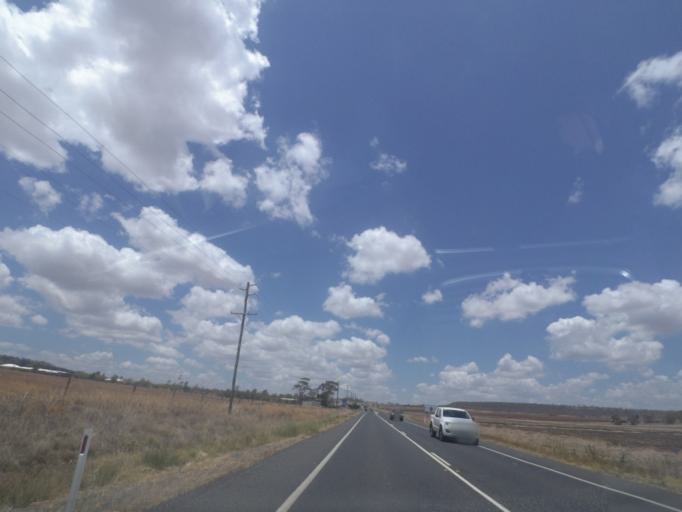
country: AU
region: Queensland
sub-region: Toowoomba
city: Top Camp
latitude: -27.7122
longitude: 151.9114
